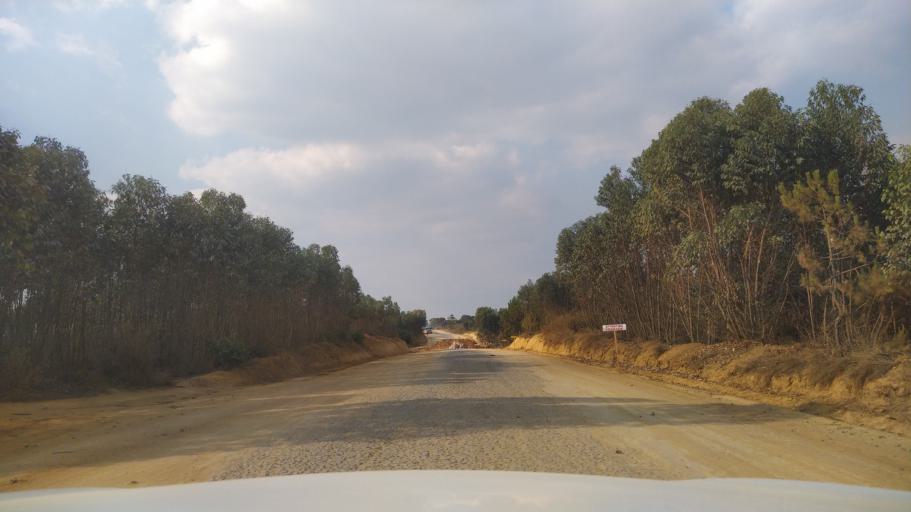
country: MG
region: Alaotra Mangoro
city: Moramanga
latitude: -18.6413
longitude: 48.2756
